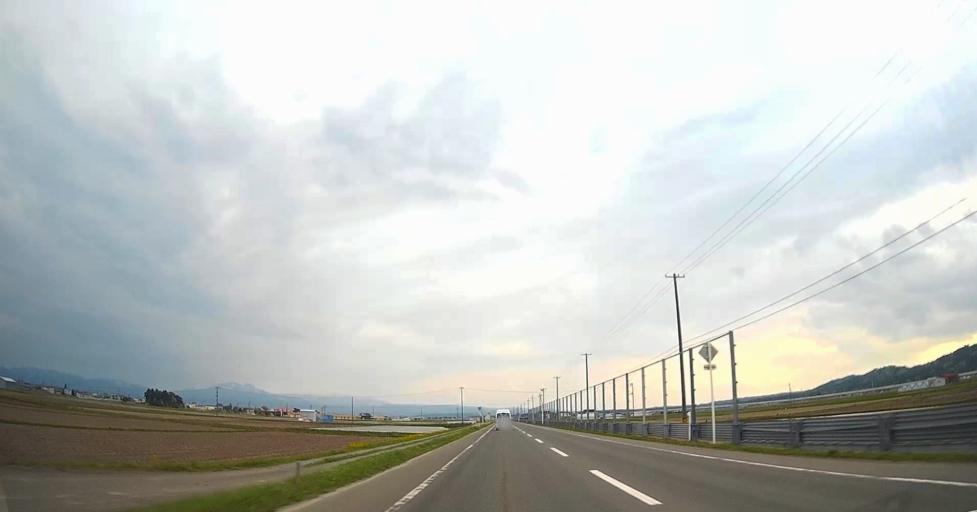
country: JP
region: Aomori
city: Aomori Shi
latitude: 40.8924
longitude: 140.6686
